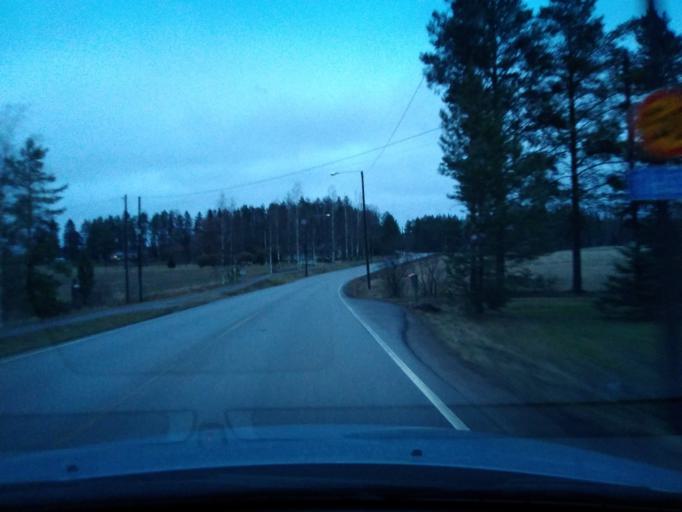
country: FI
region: Uusimaa
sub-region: Porvoo
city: Askola
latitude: 60.4972
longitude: 25.5548
